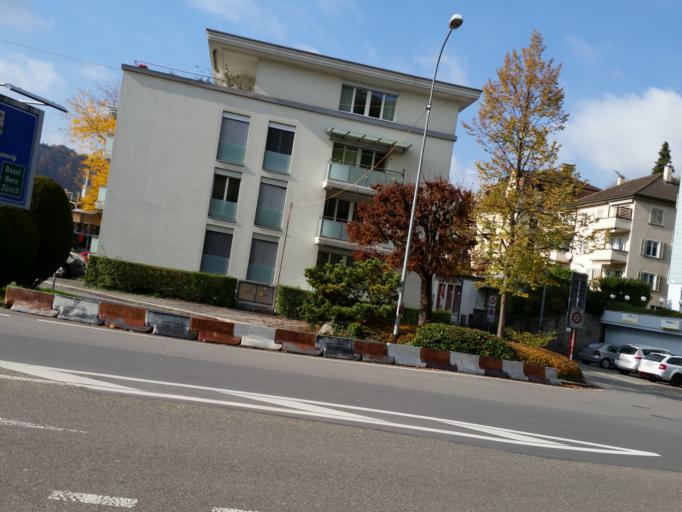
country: CH
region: Lucerne
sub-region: Lucerne-Stadt District
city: Luzern
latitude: 47.0539
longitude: 8.2995
